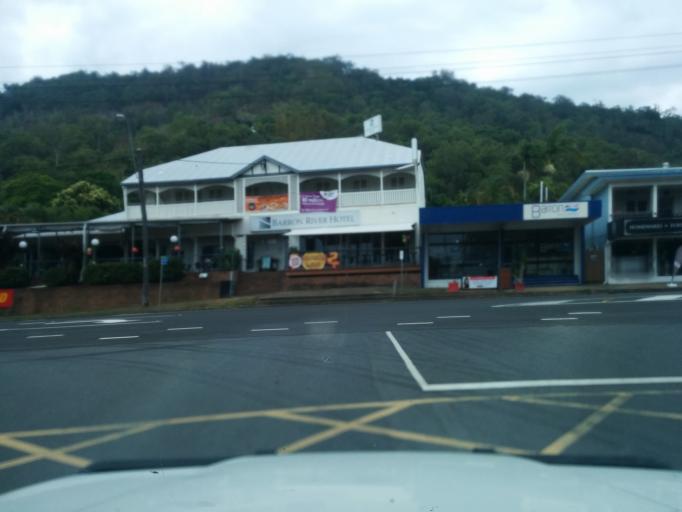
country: AU
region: Queensland
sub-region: Cairns
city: Redlynch
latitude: -16.8750
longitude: 145.7343
